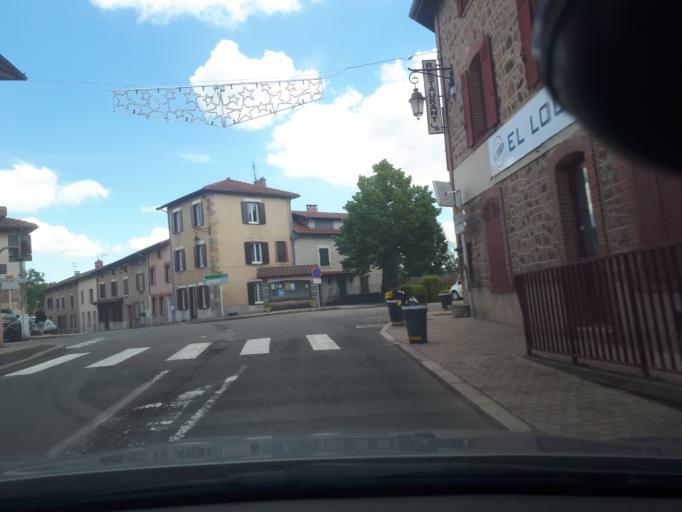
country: FR
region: Rhone-Alpes
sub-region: Departement du Rhone
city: Haute-Rivoire
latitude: 45.7188
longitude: 4.4309
